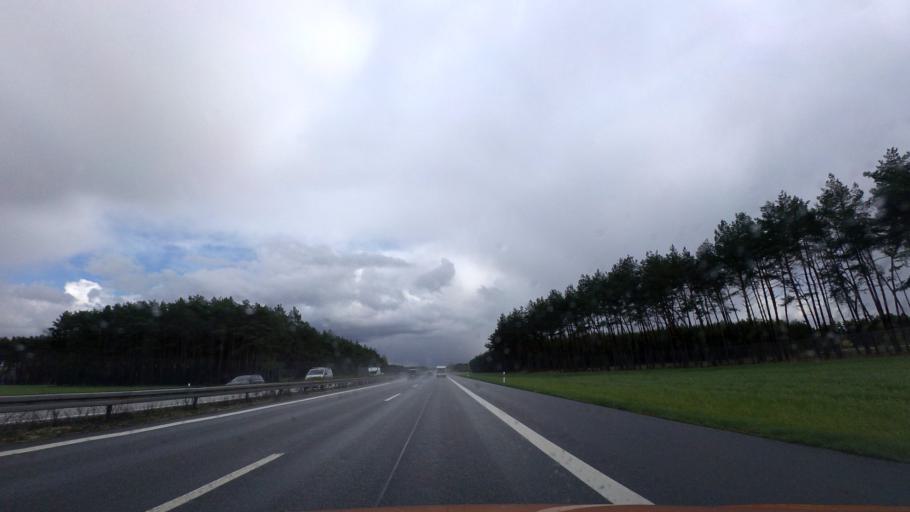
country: DE
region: Mecklenburg-Vorpommern
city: Sulstorf
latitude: 53.4548
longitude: 11.3564
